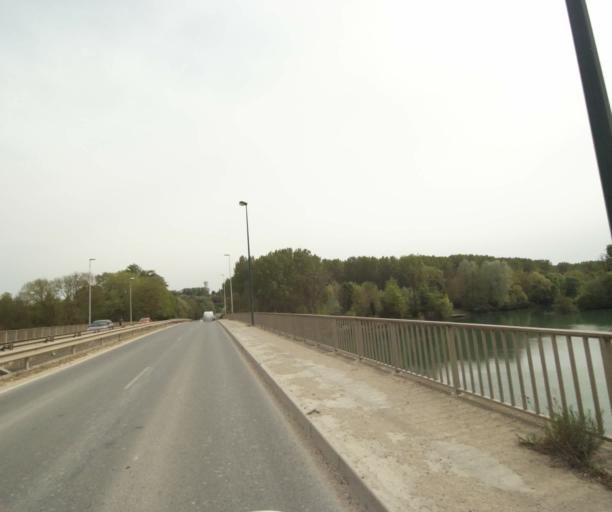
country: FR
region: Ile-de-France
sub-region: Departement de Seine-et-Marne
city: Torcy
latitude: 48.8625
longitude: 2.6440
